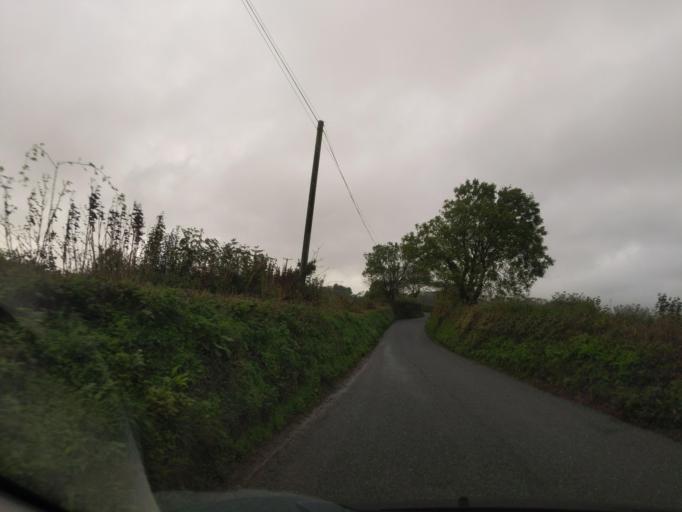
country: GB
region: England
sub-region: Cornwall
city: Saltash
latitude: 50.4521
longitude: -4.2432
